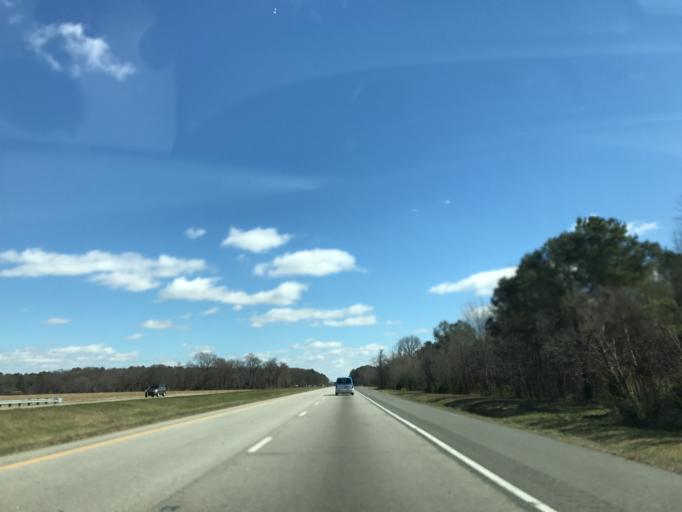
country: US
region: Maryland
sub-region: Queen Anne's County
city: Centreville
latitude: 39.0130
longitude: -76.0989
